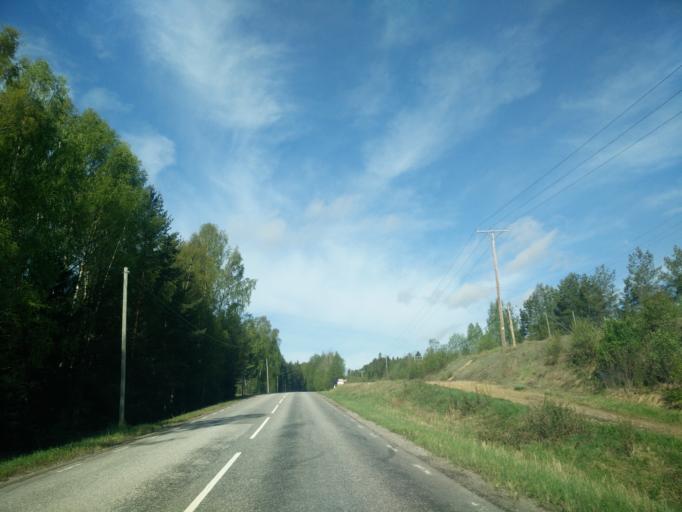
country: SE
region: Vaesternorrland
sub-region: Sundsvalls Kommun
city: Nolby
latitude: 62.2994
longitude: 17.3253
